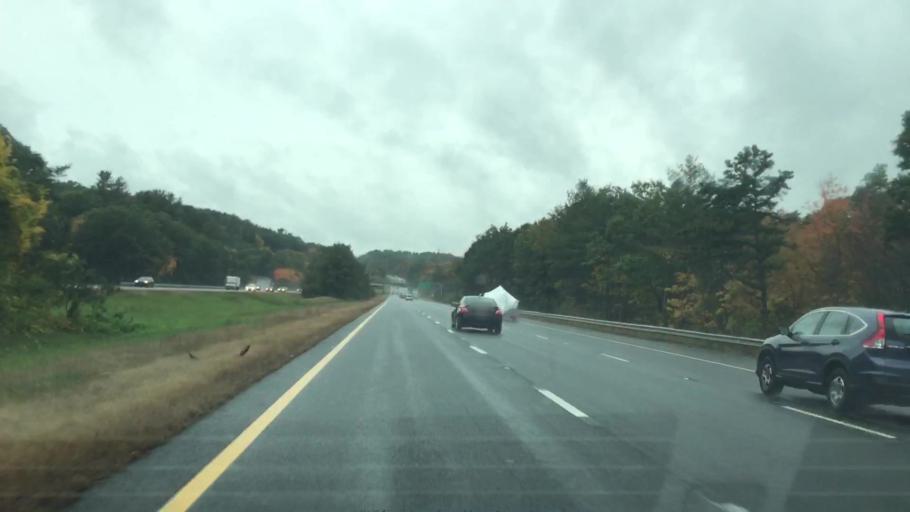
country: US
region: Massachusetts
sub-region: Essex County
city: Merrimac
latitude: 42.8326
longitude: -70.9838
